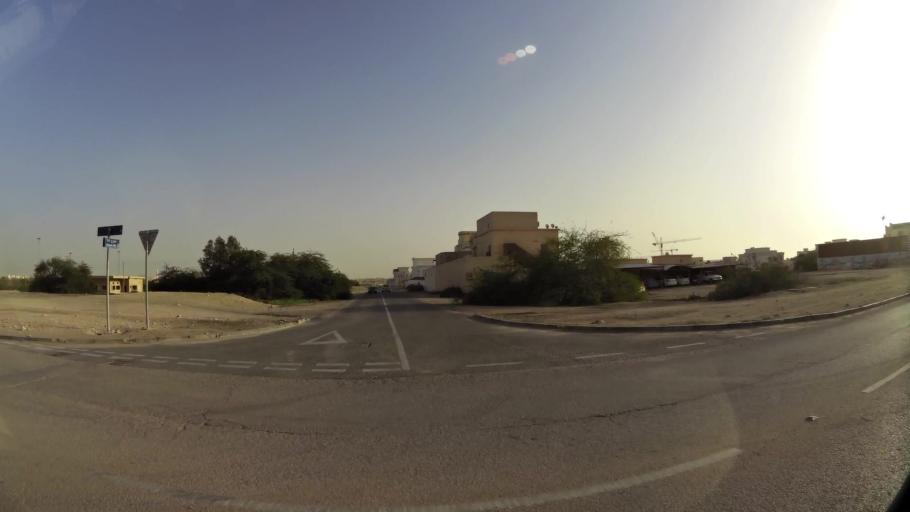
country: QA
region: Baladiyat ar Rayyan
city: Ar Rayyan
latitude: 25.3136
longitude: 51.4569
